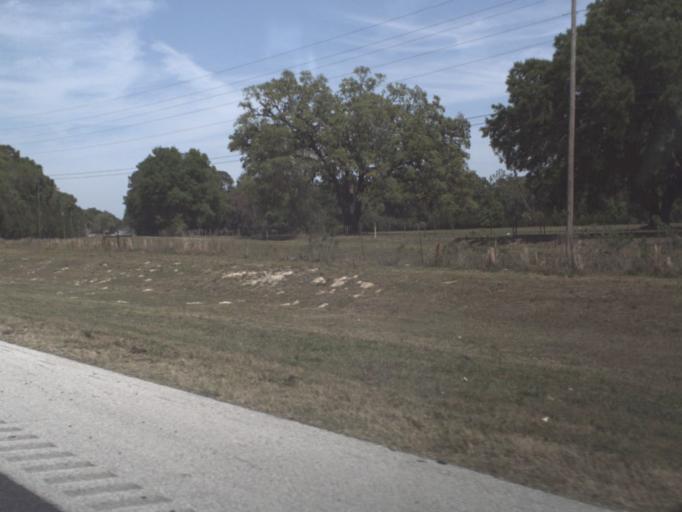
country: US
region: Florida
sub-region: Marion County
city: Belleview
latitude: 28.9531
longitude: -82.1199
